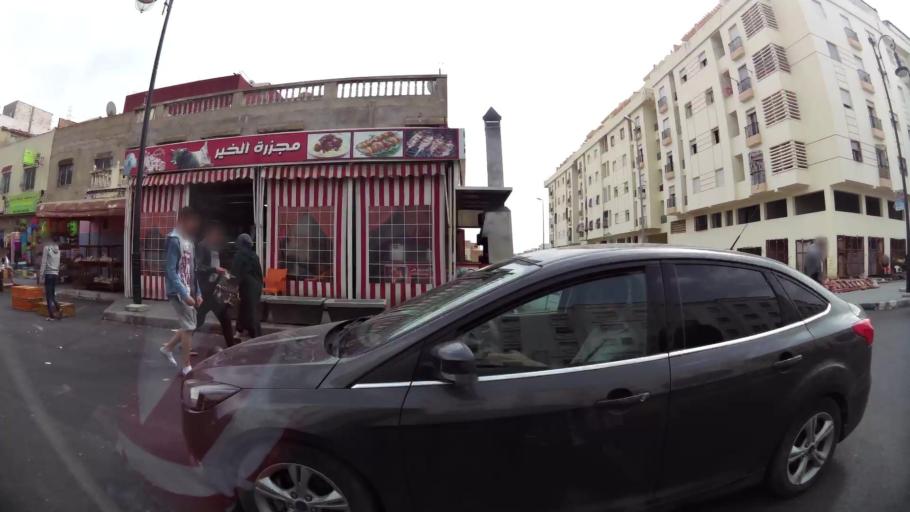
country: MA
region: Tanger-Tetouan
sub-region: Tanger-Assilah
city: Boukhalef
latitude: 35.7370
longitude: -5.8840
